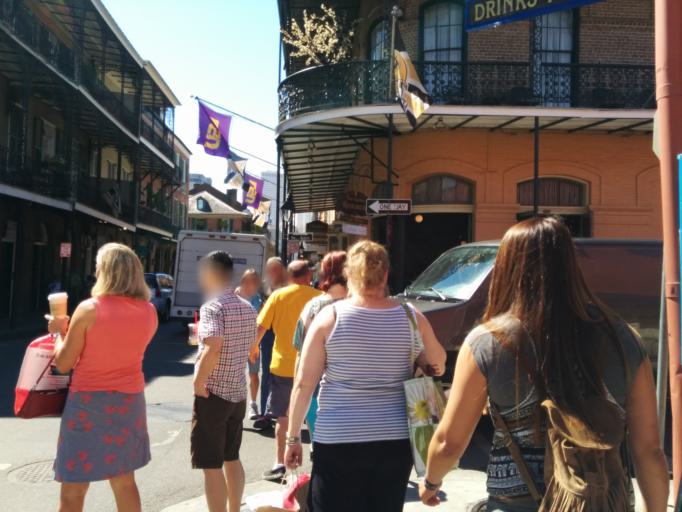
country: US
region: Louisiana
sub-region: Orleans Parish
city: New Orleans
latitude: 29.9590
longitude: -90.0639
